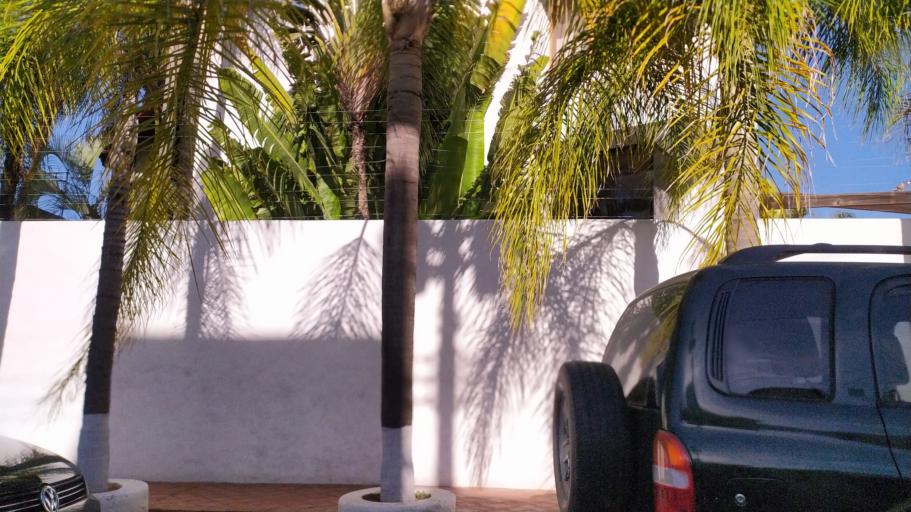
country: MX
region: Jalisco
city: Guadalajara
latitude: 20.6635
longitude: -103.4356
